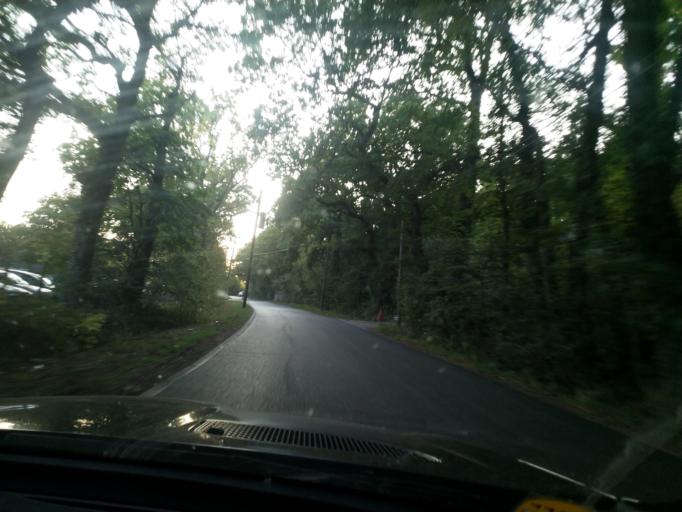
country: GB
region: England
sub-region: Kent
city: Sheerness
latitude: 51.4042
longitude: 0.7982
